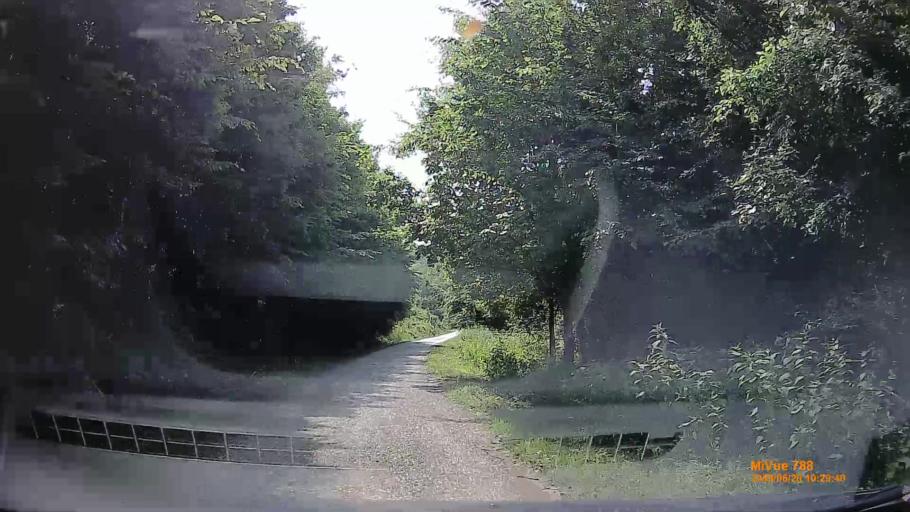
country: HU
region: Baranya
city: Mecseknadasd
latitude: 46.2077
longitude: 18.4949
